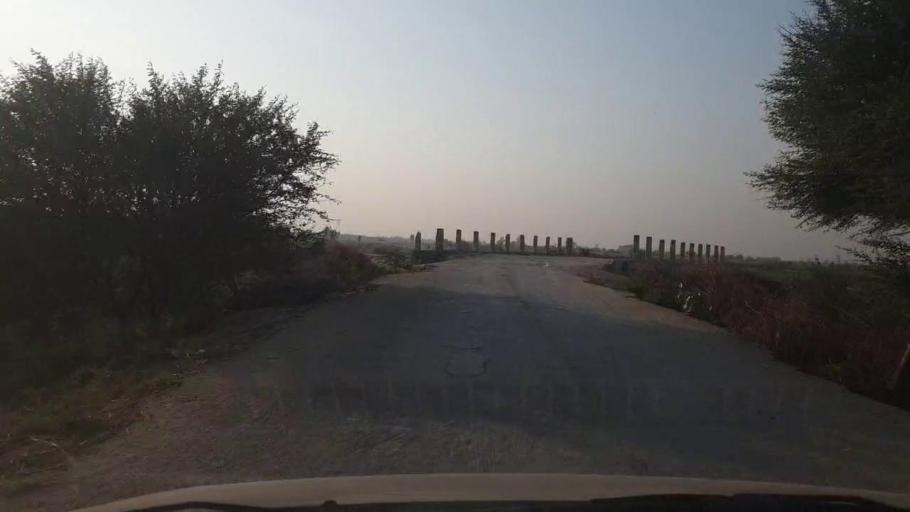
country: PK
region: Sindh
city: Mirwah Gorchani
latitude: 25.3671
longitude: 69.1383
